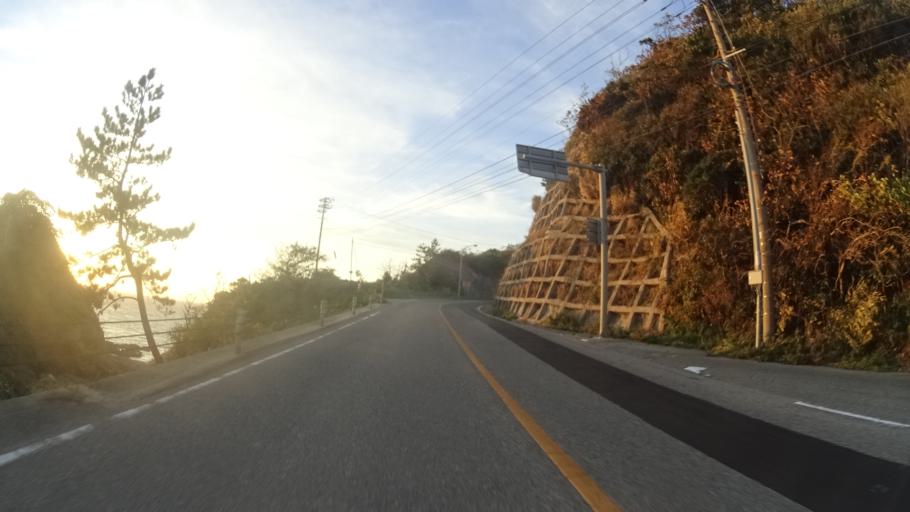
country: JP
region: Ishikawa
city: Nanao
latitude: 37.2196
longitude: 136.6981
